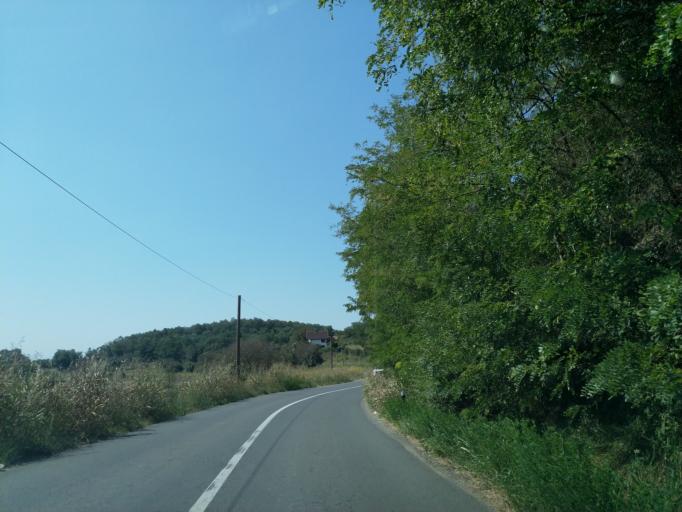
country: RS
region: Central Serbia
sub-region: Rasinski Okrug
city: Krusevac
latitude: 43.6221
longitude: 21.3267
